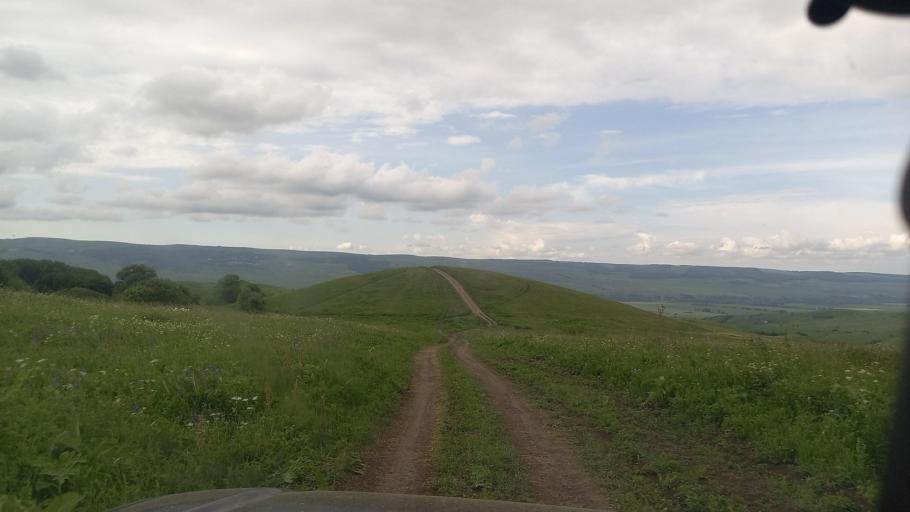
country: RU
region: Krasnodarskiy
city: Peredovaya
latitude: 44.0586
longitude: 41.3631
